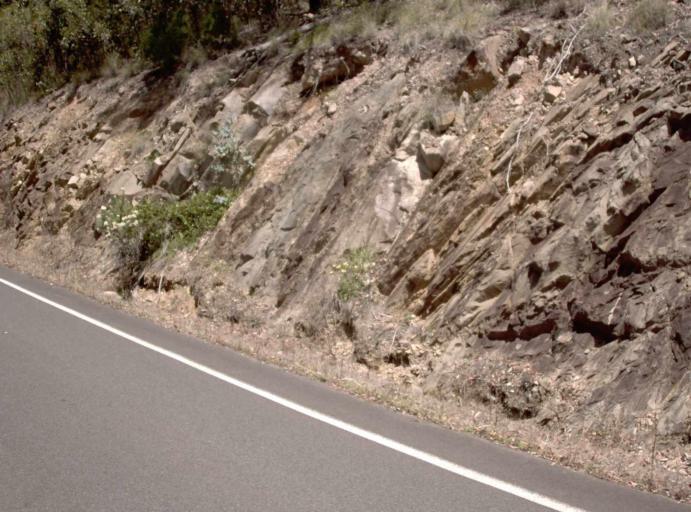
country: AU
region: Victoria
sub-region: East Gippsland
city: Lakes Entrance
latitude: -37.6157
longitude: 147.8829
